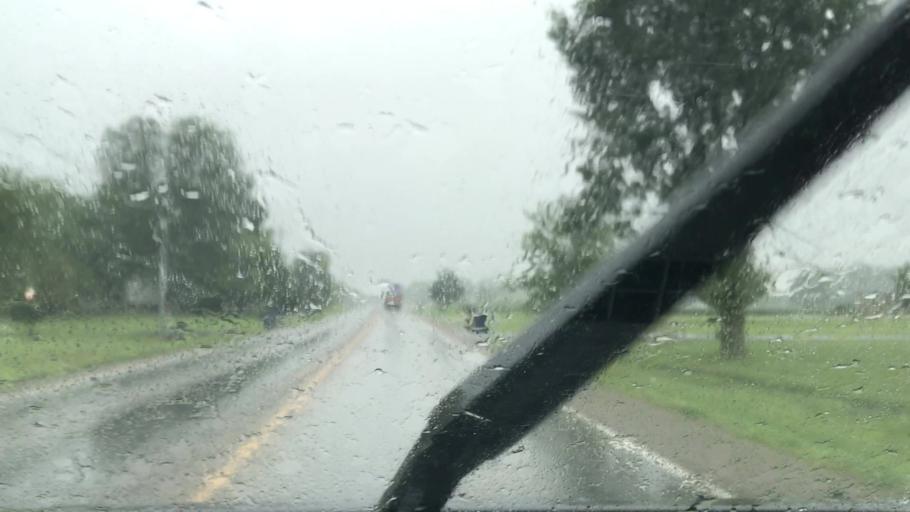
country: US
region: Indiana
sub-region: Hamilton County
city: Sheridan
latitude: 40.1262
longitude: -86.2016
